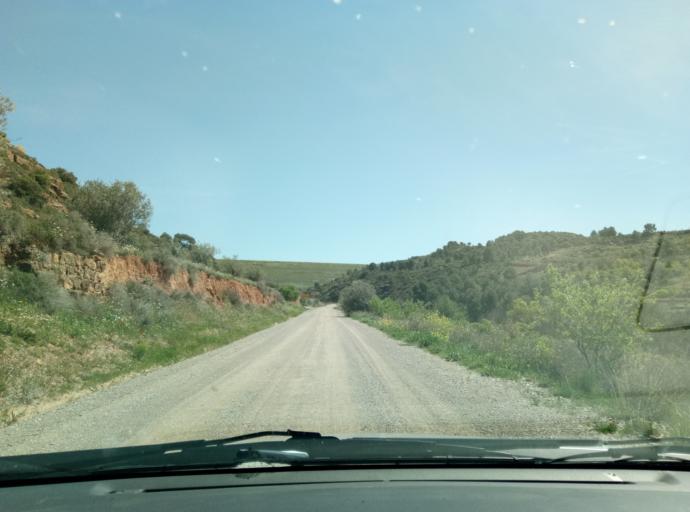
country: ES
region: Catalonia
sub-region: Provincia de Lleida
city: el Cogul
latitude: 41.4517
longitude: 0.7475
